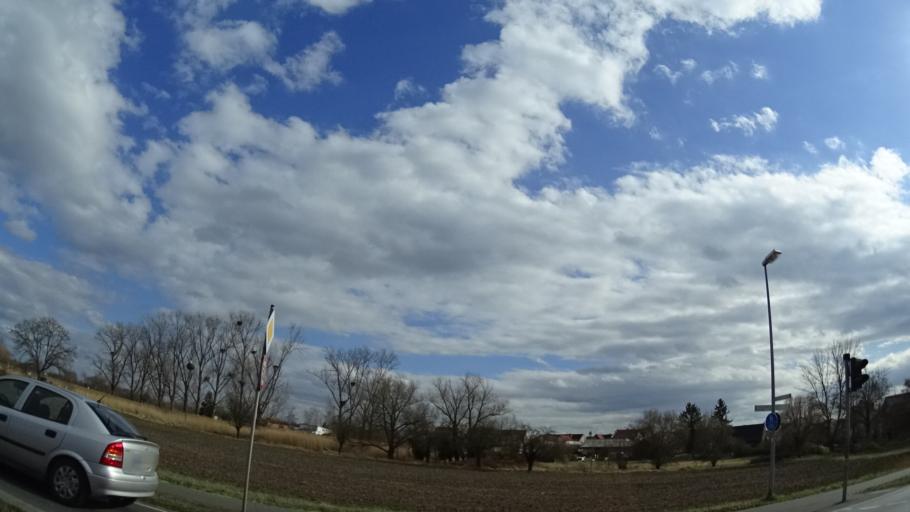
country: DE
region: Hesse
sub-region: Regierungsbezirk Darmstadt
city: Gross-Gerau
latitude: 49.9018
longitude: 8.4806
